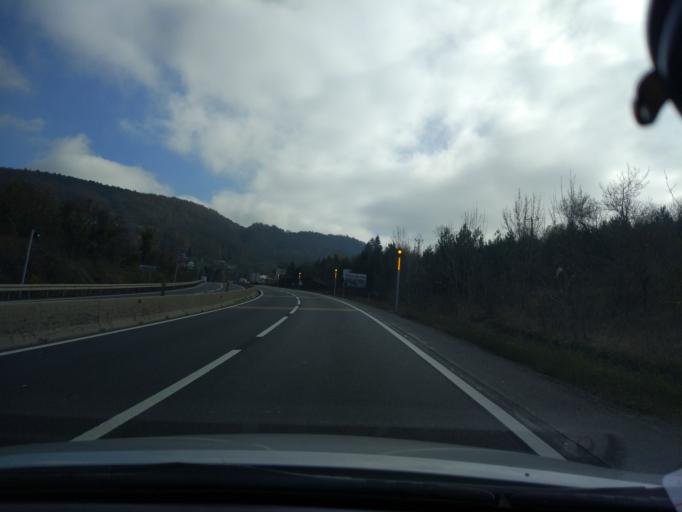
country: TR
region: Duzce
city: Kaynasli
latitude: 40.7480
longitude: 31.3773
